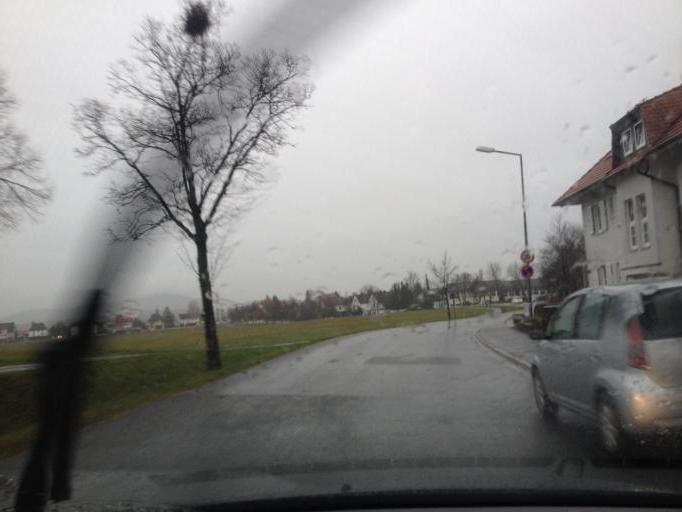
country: DE
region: Bavaria
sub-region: Regierungsbezirk Mittelfranken
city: Lauf an der Pegnitz
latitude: 49.5187
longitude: 11.2747
